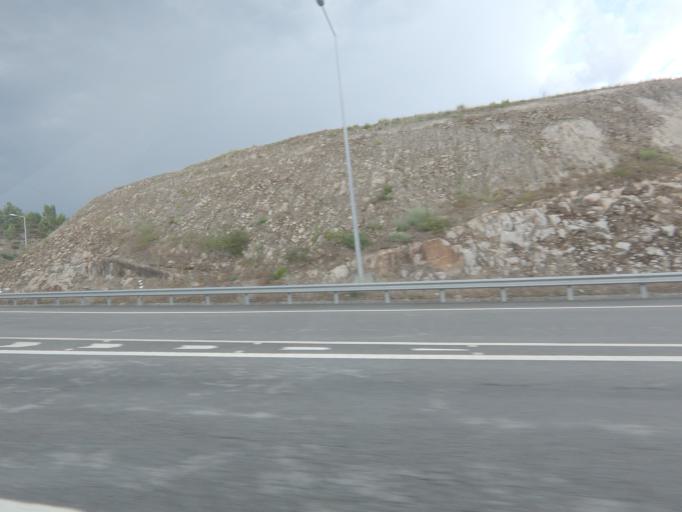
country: PT
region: Viseu
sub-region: Viseu
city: Abraveses
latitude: 40.6771
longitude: -7.9681
